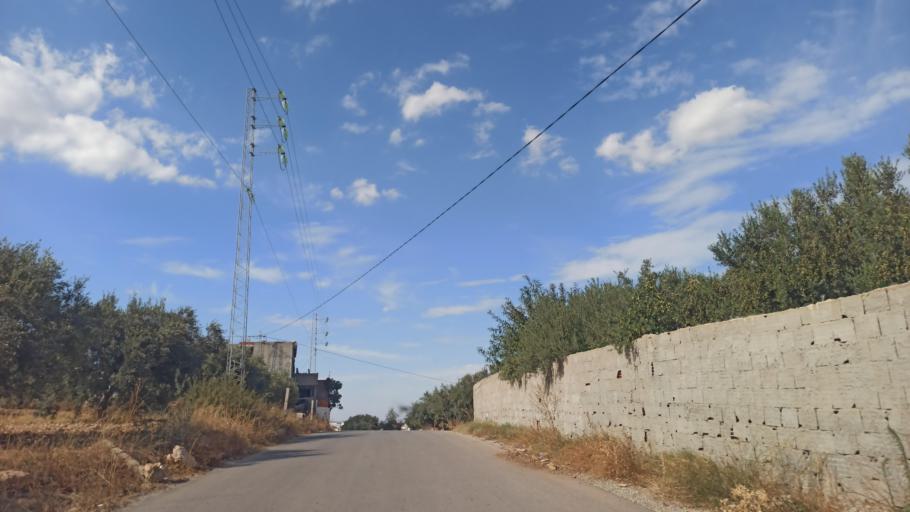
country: TN
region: Zaghwan
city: Zaghouan
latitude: 36.3352
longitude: 10.2118
